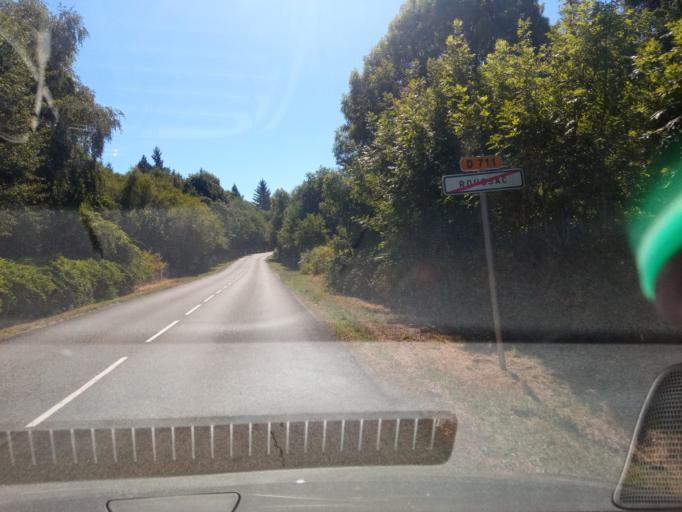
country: FR
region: Limousin
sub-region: Departement de la Haute-Vienne
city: Nantiat
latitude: 46.0736
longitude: 1.2026
